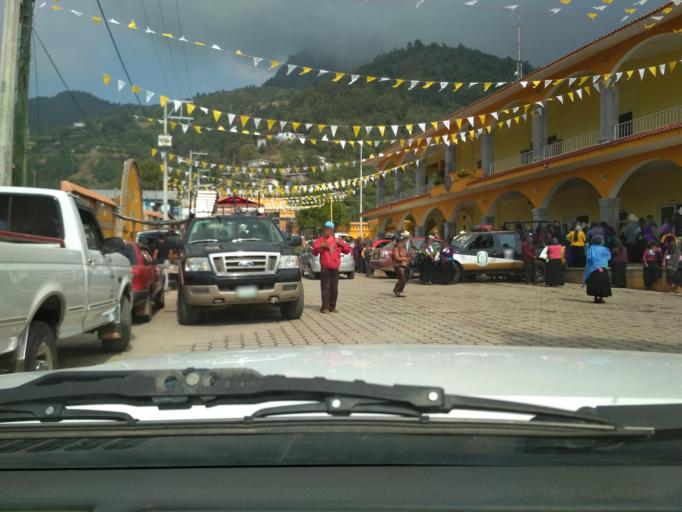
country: MX
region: Veracruz
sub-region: Soledad Atzompa
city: Tlatilpa
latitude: 18.7553
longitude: -97.1516
